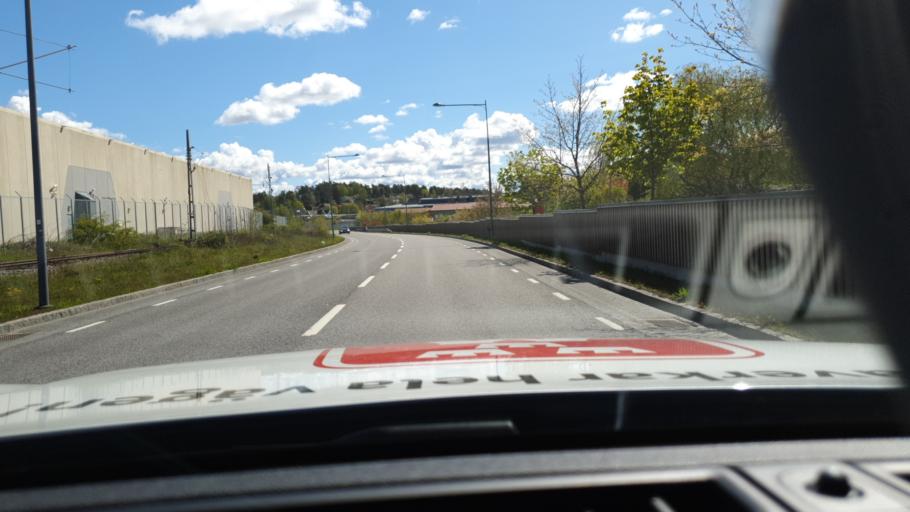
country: SE
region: Stockholm
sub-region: Jarfalla Kommun
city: Jakobsberg
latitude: 59.3874
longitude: 17.8840
